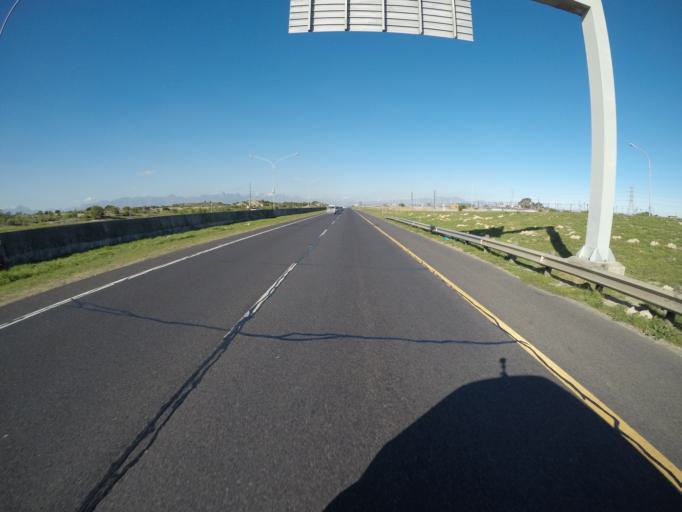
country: ZA
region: Western Cape
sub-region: City of Cape Town
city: Lansdowne
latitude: -34.0135
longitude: 18.6608
